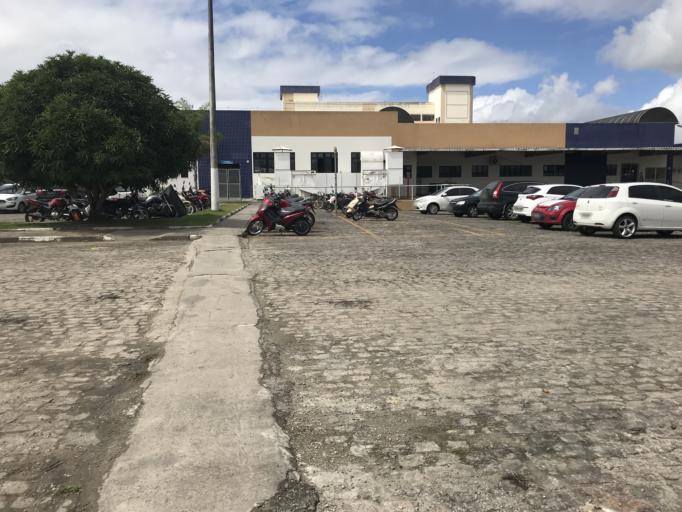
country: BR
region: Bahia
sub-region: Santo Antonio De Jesus
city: Santo Antonio de Jesus
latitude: -12.9798
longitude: -39.2823
